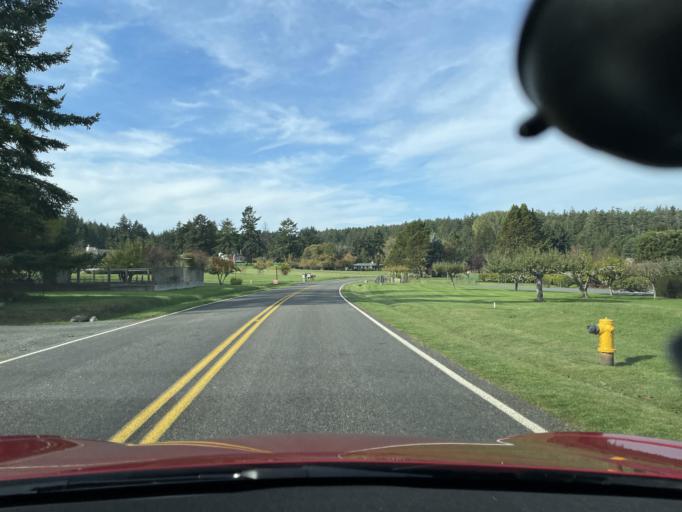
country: US
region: Washington
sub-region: San Juan County
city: Friday Harbor
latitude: 48.5265
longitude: -122.9789
